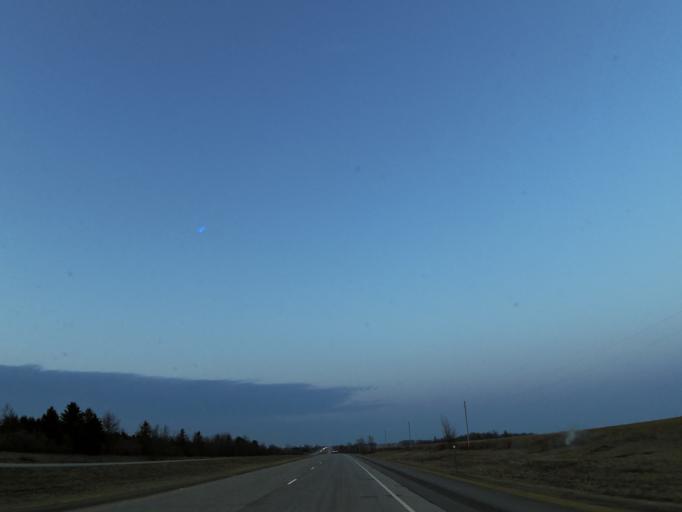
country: US
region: Minnesota
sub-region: Mower County
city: Grand Meadow
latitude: 43.7568
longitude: -92.6466
